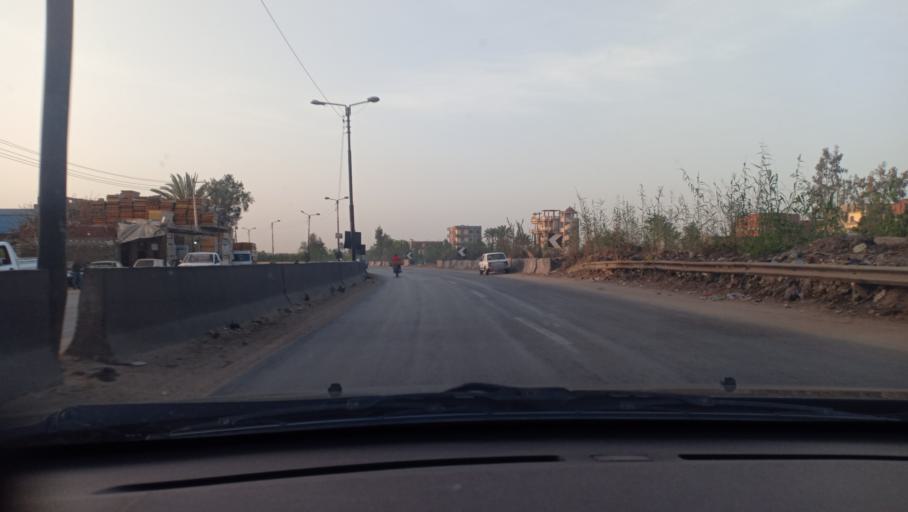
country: EG
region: Muhafazat al Gharbiyah
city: Zifta
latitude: 30.6713
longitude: 31.2859
